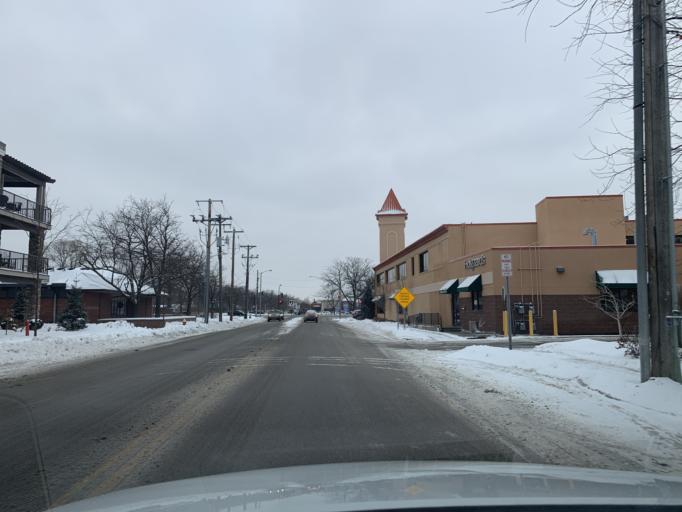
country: US
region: Minnesota
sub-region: Hennepin County
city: Saint Louis Park
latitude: 44.9298
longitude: -93.3473
